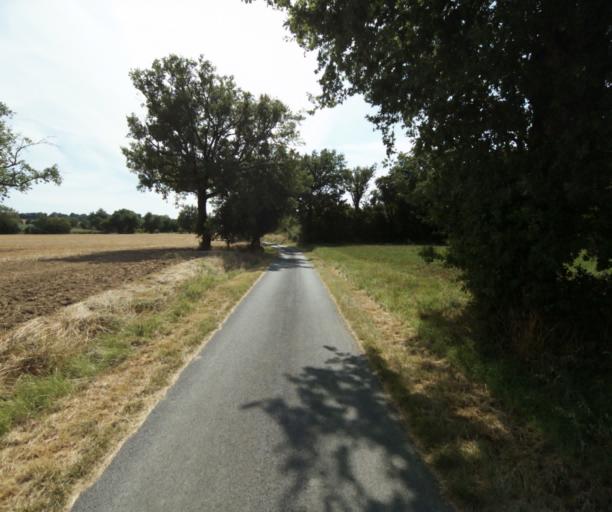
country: FR
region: Midi-Pyrenees
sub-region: Departement du Tarn
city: Soreze
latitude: 43.5043
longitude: 2.0687
